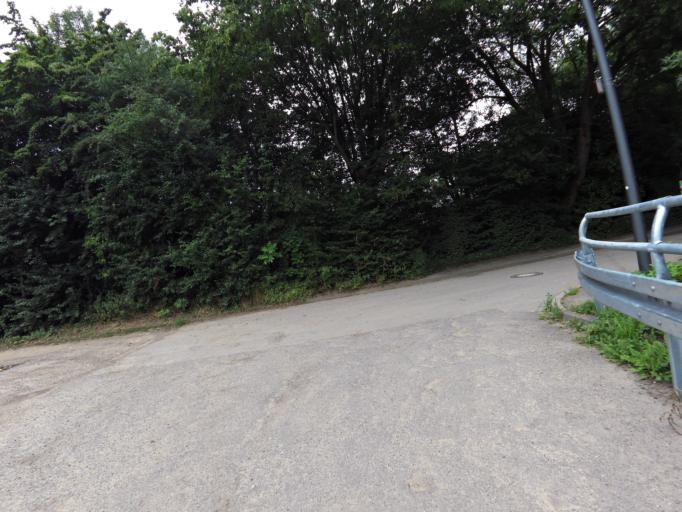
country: NL
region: Limburg
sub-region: Gemeente Vaals
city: Vaals
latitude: 50.8130
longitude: 6.0354
